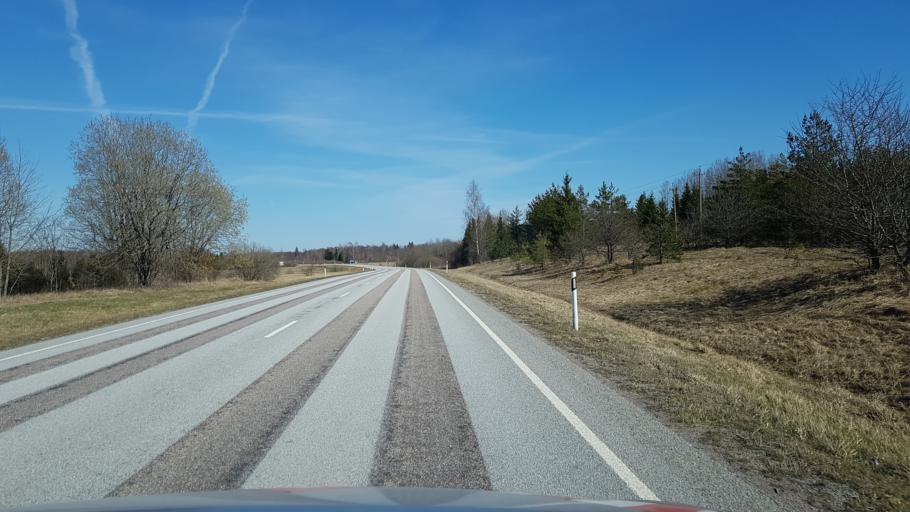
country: EE
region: Laeaene
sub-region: Lihula vald
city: Lihula
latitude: 58.6674
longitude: 23.7548
